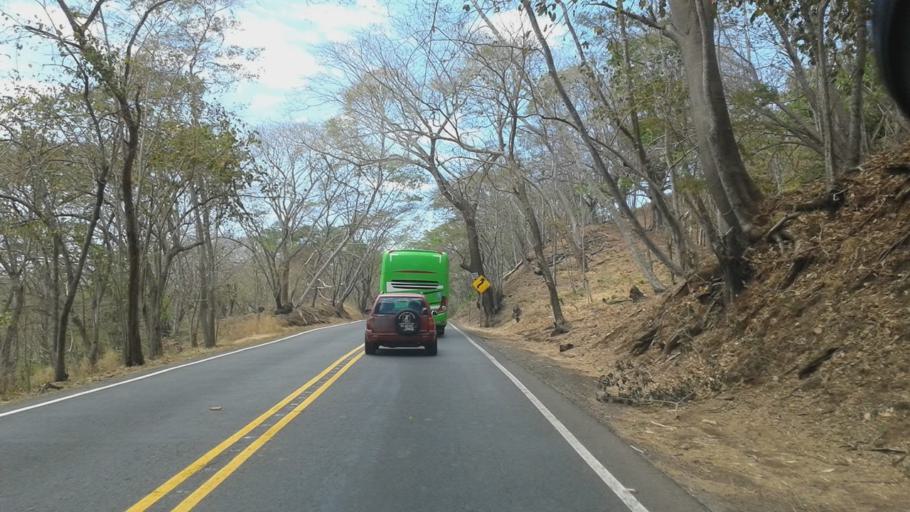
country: CR
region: Puntarenas
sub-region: Canton Central de Puntarenas
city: Puntarenas
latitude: 10.1186
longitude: -84.8969
